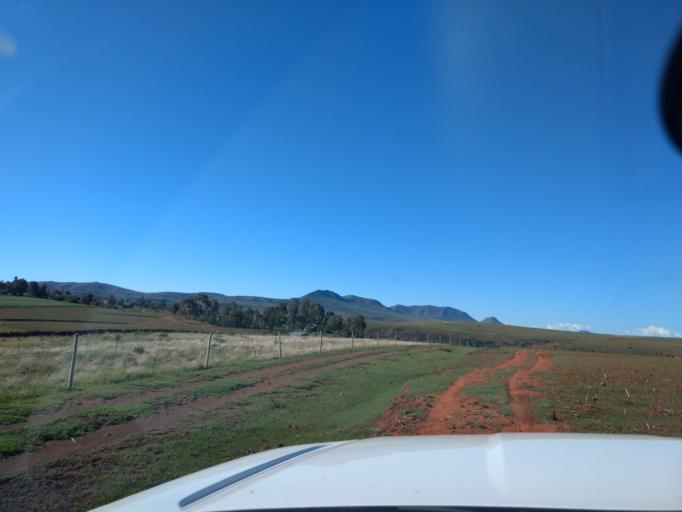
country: LS
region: Berea
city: Teyateyaneng
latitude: -29.3688
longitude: 27.7845
